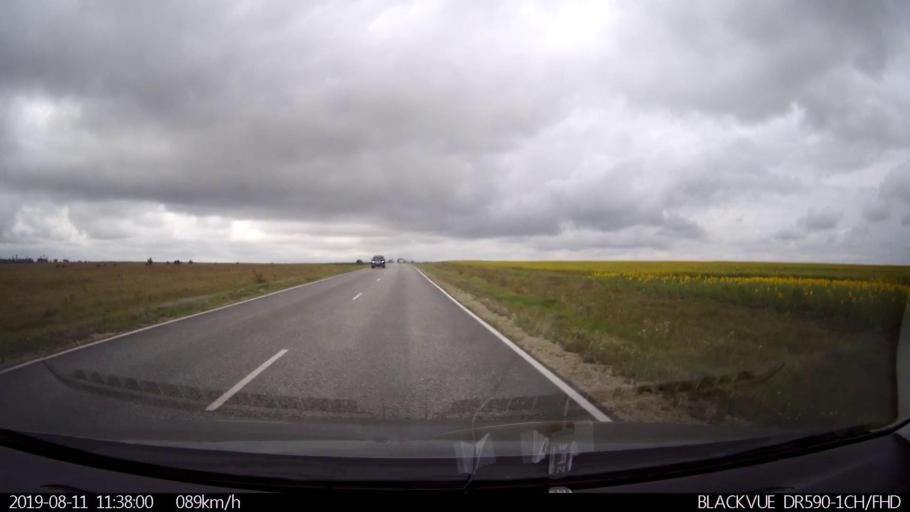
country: RU
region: Ulyanovsk
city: Silikatnyy
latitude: 53.9982
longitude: 48.1837
